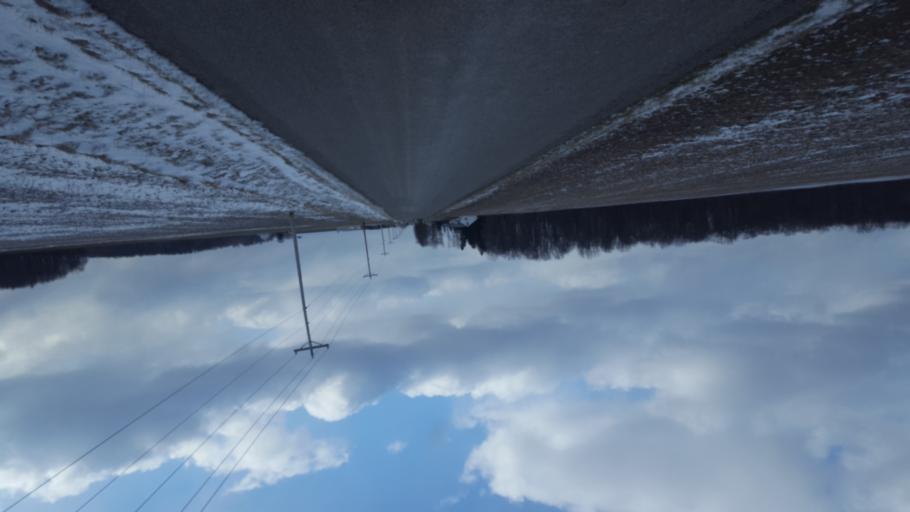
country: US
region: Ohio
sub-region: Morrow County
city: Mount Gilead
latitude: 40.6125
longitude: -82.7285
